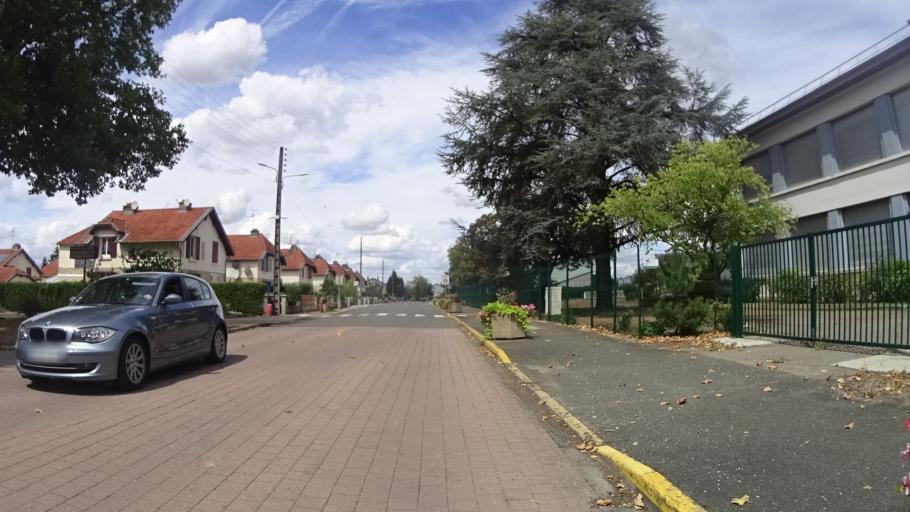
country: FR
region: Franche-Comte
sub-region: Departement du Jura
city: Damparis
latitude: 47.0680
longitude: 5.4142
